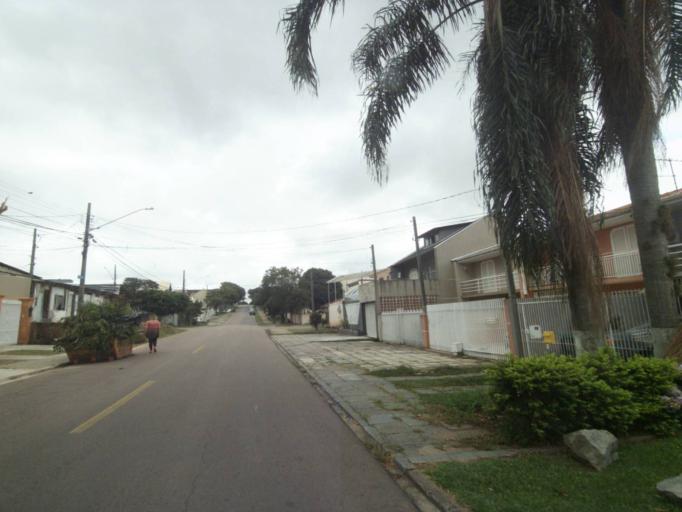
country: BR
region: Parana
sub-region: Pinhais
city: Pinhais
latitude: -25.4564
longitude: -49.2196
